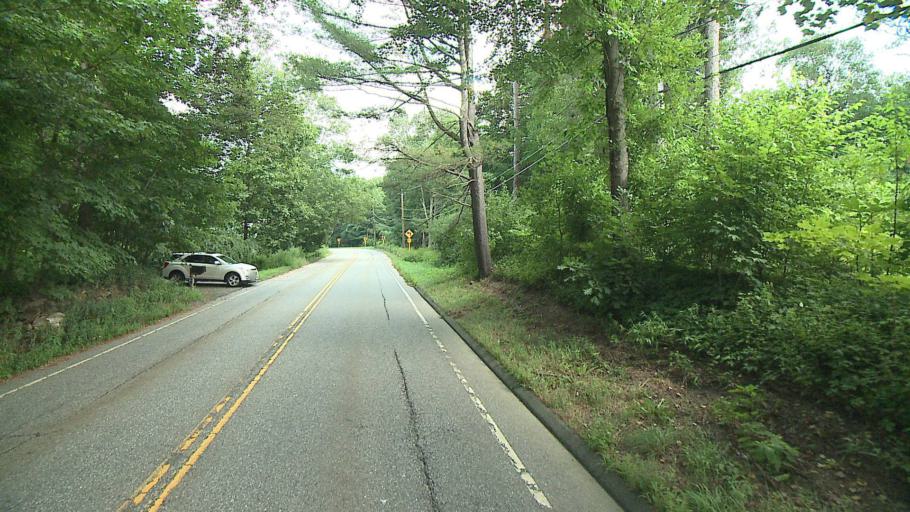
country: US
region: Connecticut
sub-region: Litchfield County
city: Bethlehem Village
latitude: 41.6741
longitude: -73.1578
